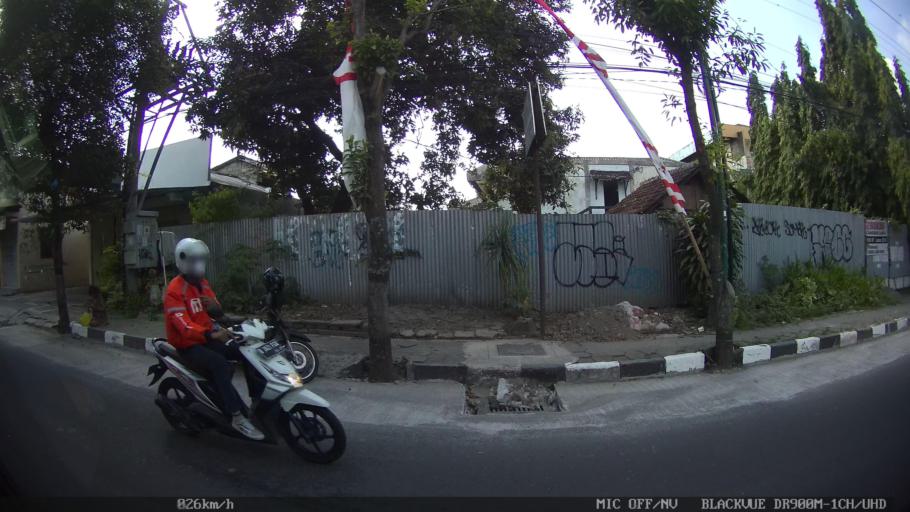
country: ID
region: Daerah Istimewa Yogyakarta
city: Yogyakarta
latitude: -7.8214
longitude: 110.3731
